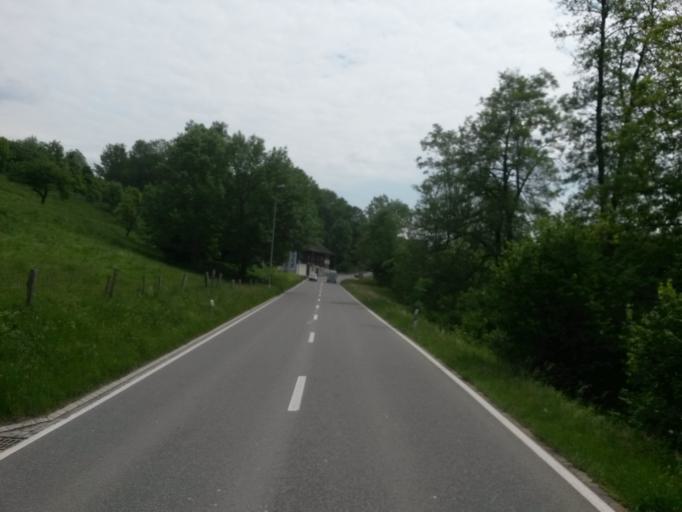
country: CH
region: Zurich
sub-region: Bezirk Pfaeffikon
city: Illnau
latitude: 47.4205
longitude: 8.7164
